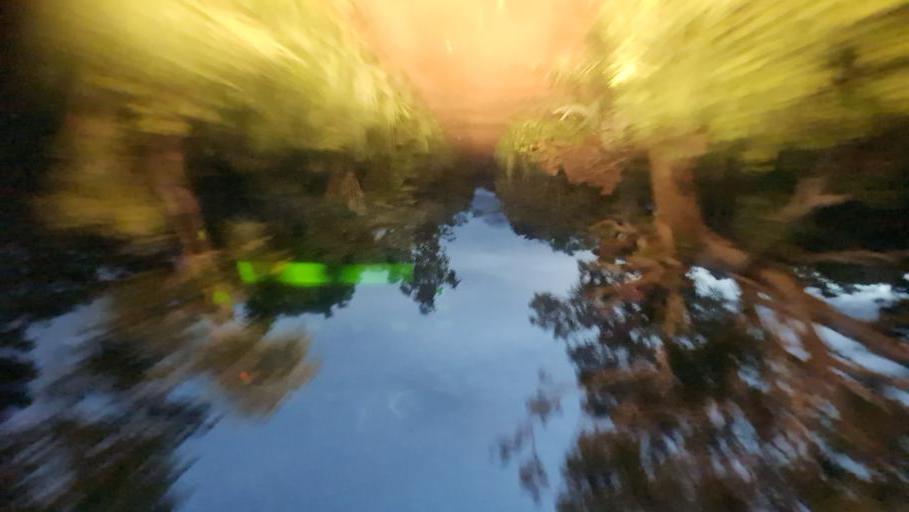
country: MZ
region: Nampula
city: Nampula
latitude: -14.6827
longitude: 39.8334
